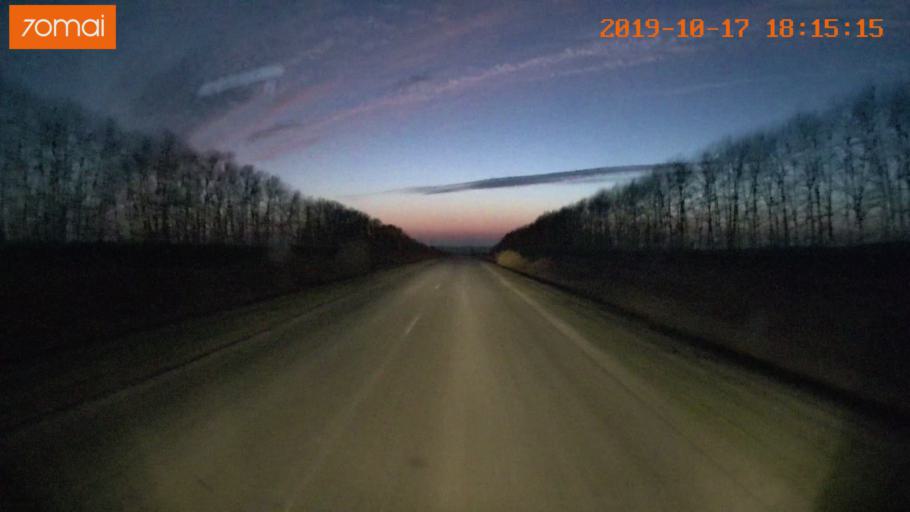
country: RU
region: Tula
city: Kurkino
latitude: 53.4047
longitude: 38.5406
